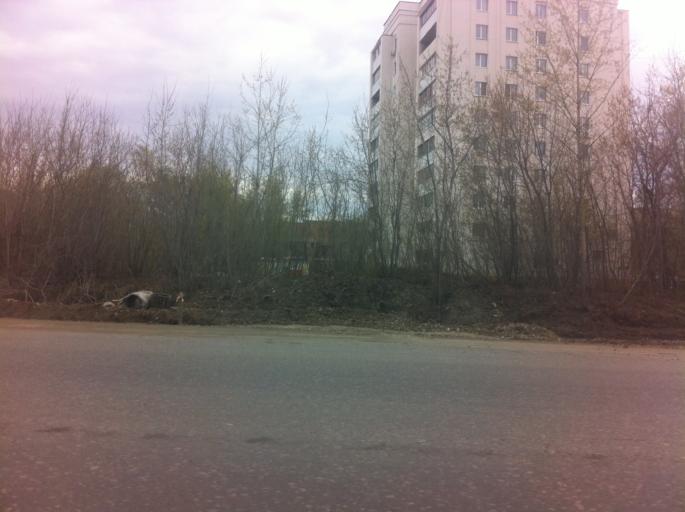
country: RU
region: Samara
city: Volzhskiy
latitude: 53.3510
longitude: 50.2168
